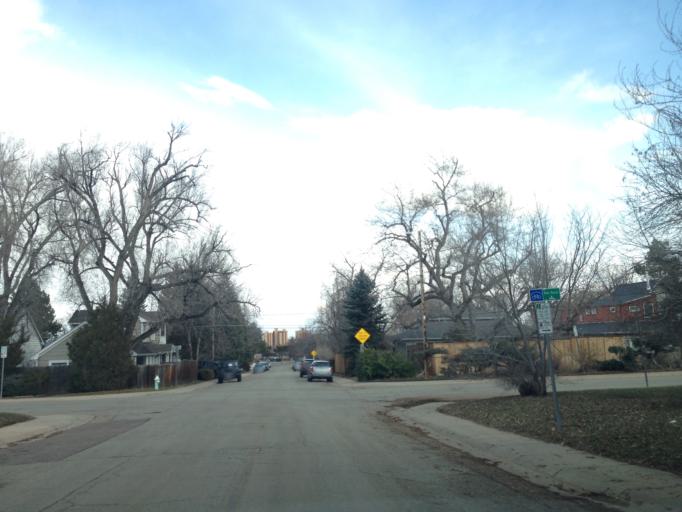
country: US
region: Colorado
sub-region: Boulder County
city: Boulder
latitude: 39.9991
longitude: -105.2655
